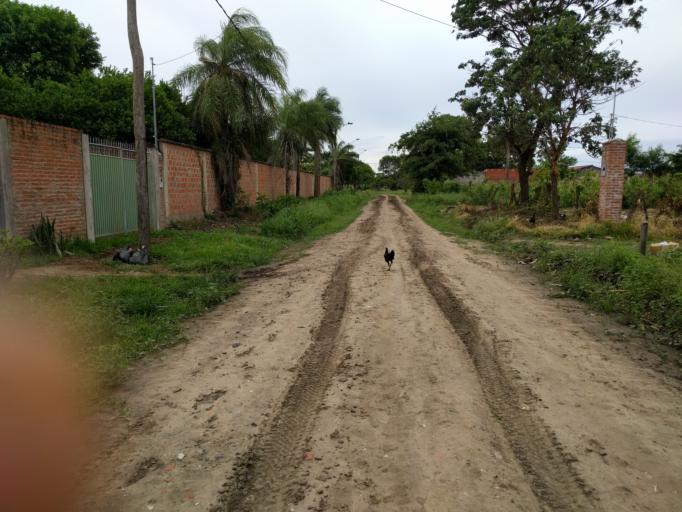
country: BO
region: Santa Cruz
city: Santa Cruz de la Sierra
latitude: -17.8479
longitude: -63.2342
